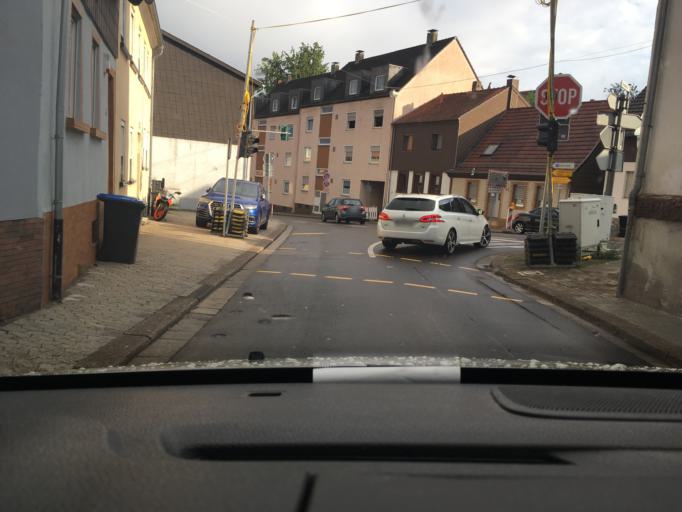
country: DE
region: Saarland
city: Sankt Ingbert
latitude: 49.2837
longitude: 7.1126
